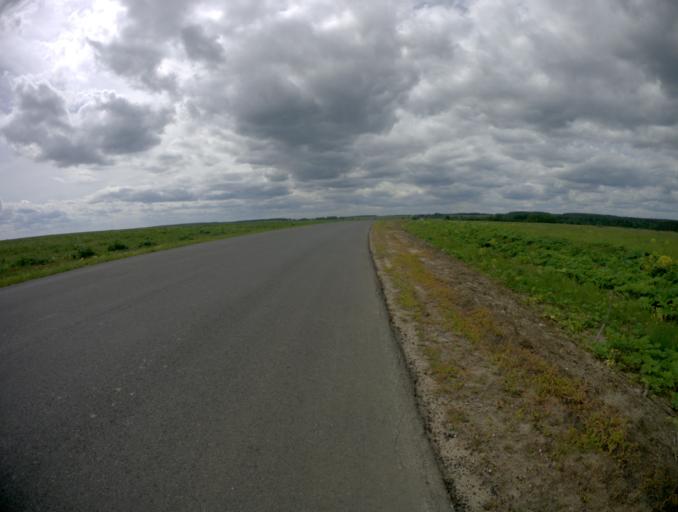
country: RU
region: Vladimir
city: Stavrovo
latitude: 56.2757
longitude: 39.8375
